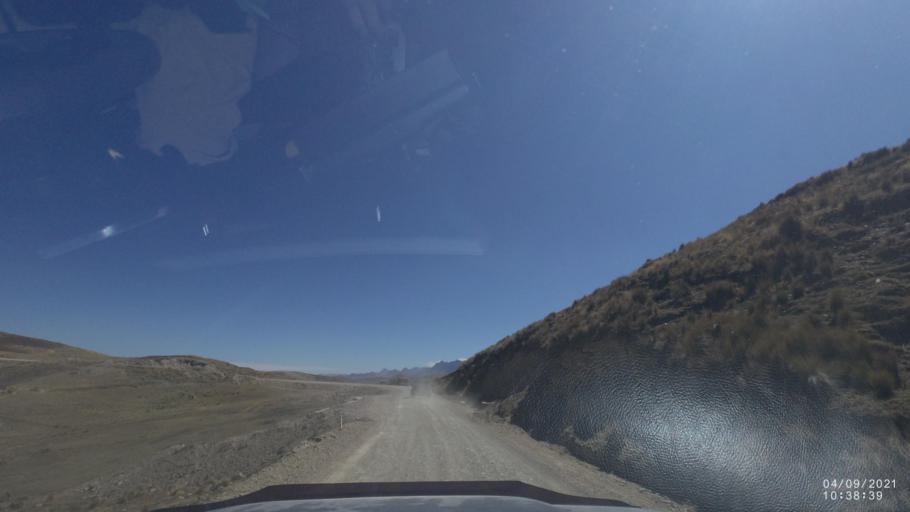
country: BO
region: Cochabamba
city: Sipe Sipe
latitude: -17.2856
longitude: -66.4580
